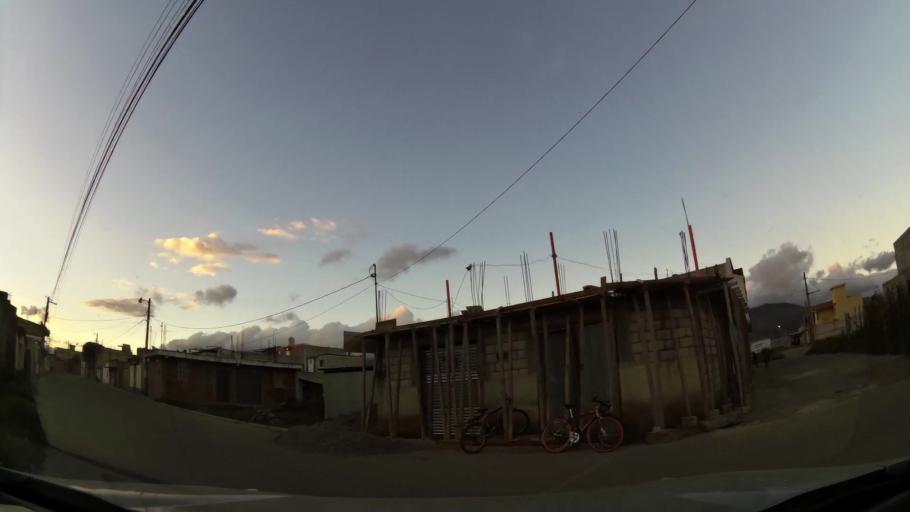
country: GT
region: Quetzaltenango
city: Quetzaltenango
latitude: 14.8538
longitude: -91.5105
